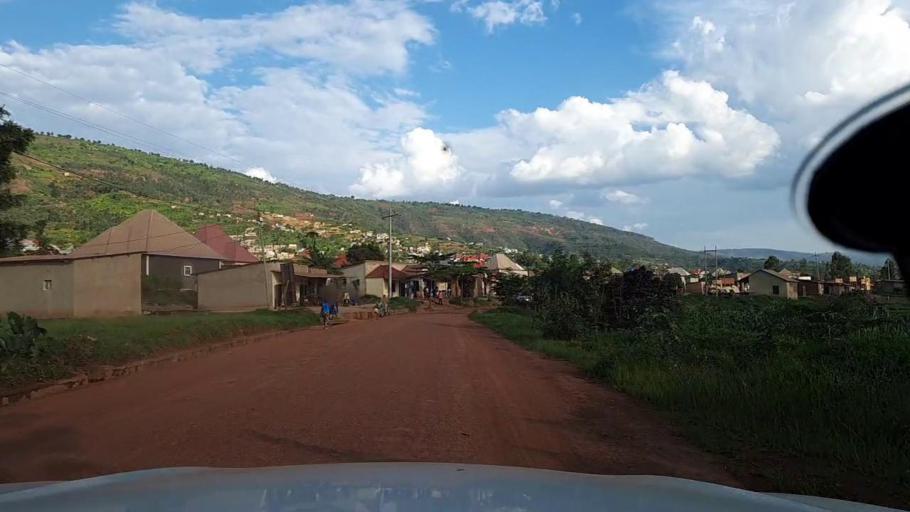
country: RW
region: Kigali
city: Kigali
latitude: -1.9059
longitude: 29.9791
